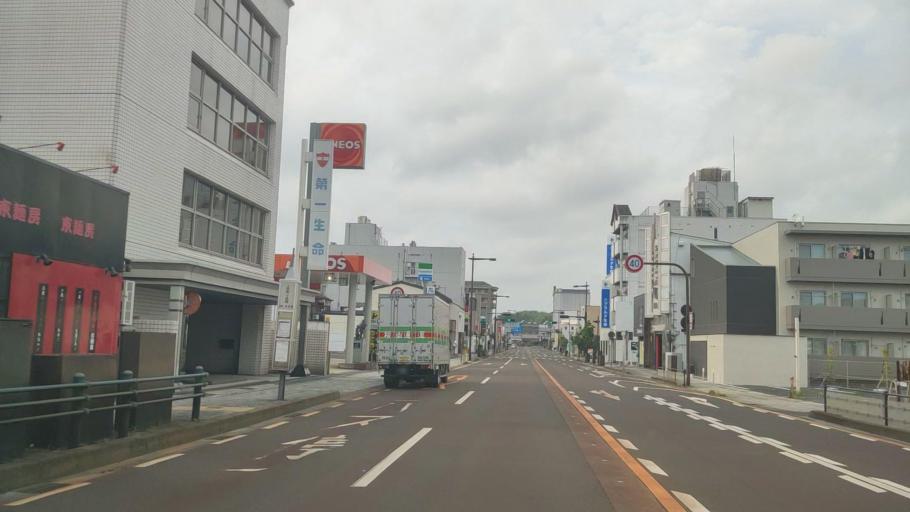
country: JP
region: Tottori
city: Kurayoshi
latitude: 35.4509
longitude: 133.8494
